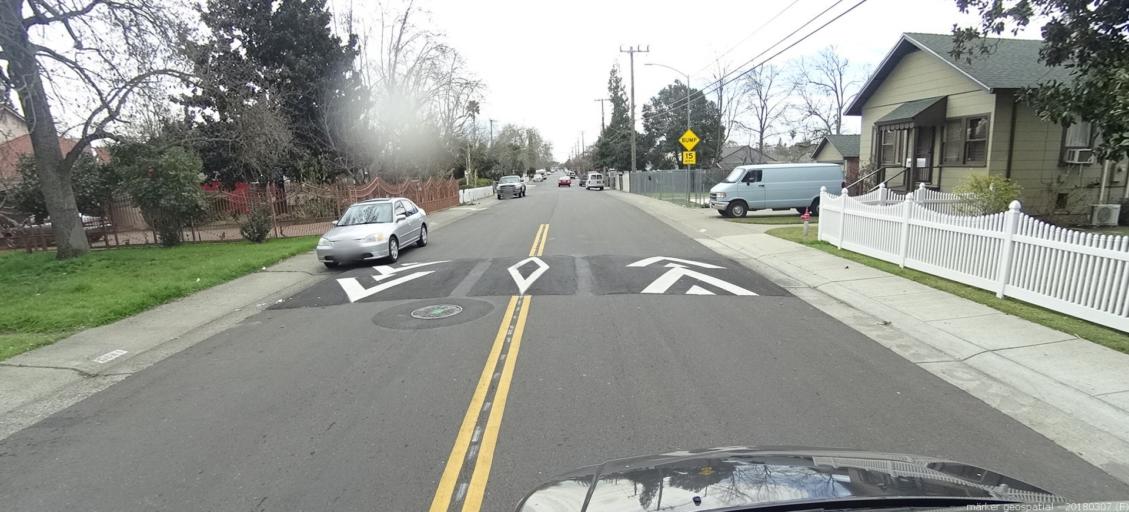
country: US
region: California
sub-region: Sacramento County
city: Parkway
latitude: 38.5293
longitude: -121.4589
